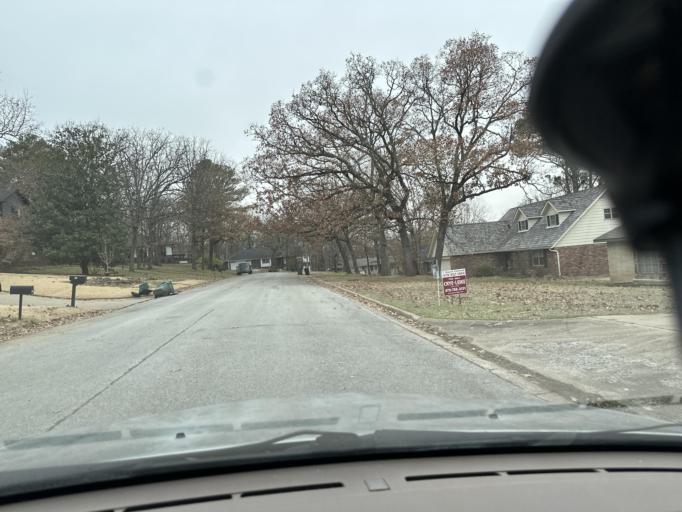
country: US
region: Arkansas
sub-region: Washington County
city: Johnson
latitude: 36.1040
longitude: -94.1436
